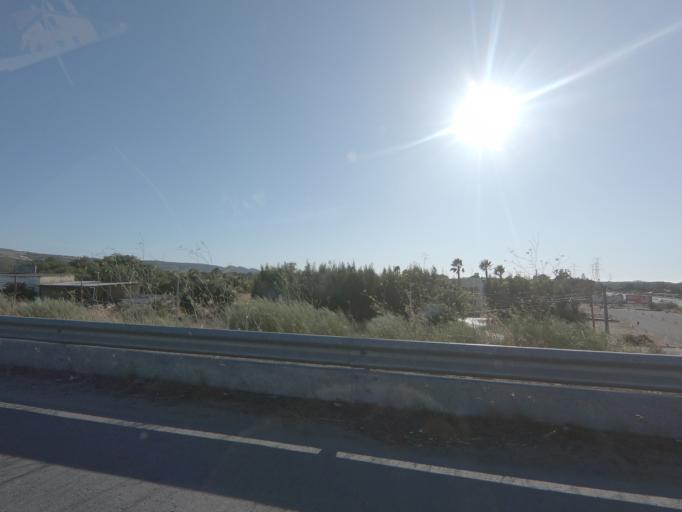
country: PT
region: Setubal
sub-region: Palmela
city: Palmela
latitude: 38.5848
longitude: -8.9162
